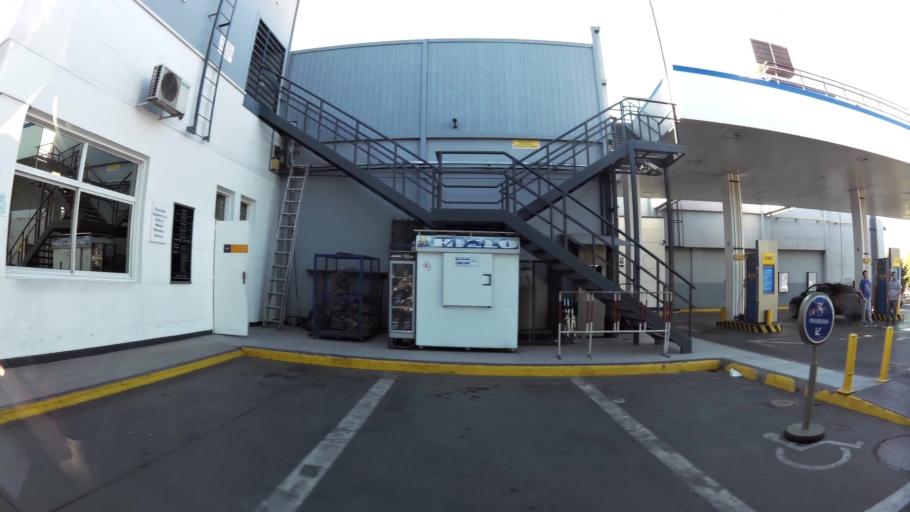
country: AR
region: Mendoza
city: Mendoza
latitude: -32.8994
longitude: -68.8360
